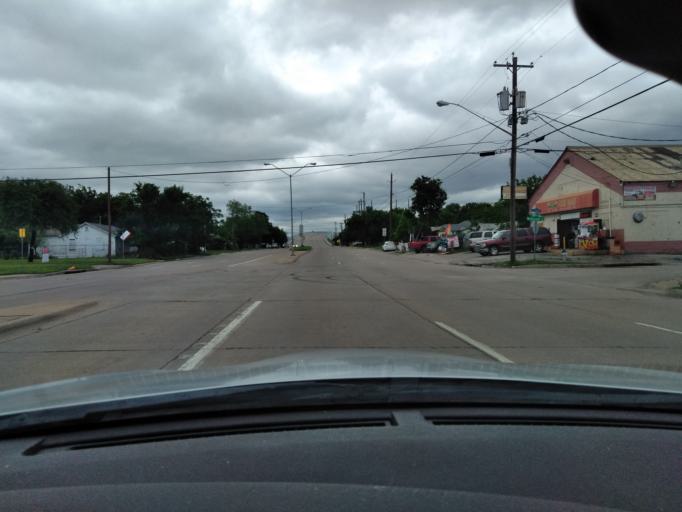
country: US
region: Texas
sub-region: Dallas County
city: Dallas
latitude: 32.7819
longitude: -96.8358
